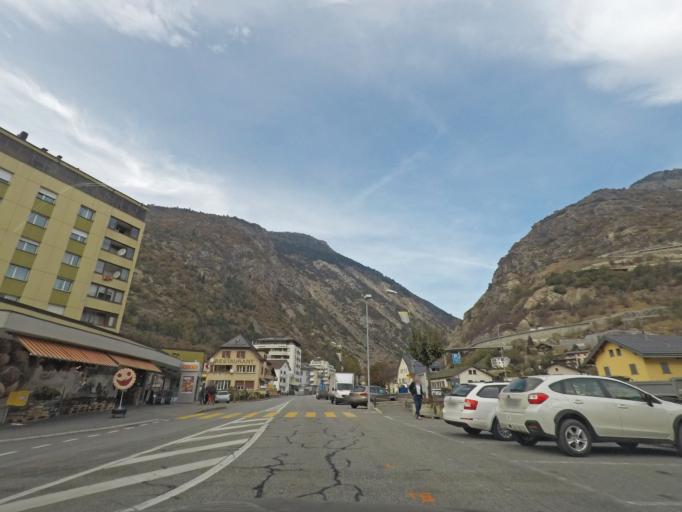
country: CH
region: Valais
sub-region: Leuk District
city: Gampel
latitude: 46.3148
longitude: 7.7446
